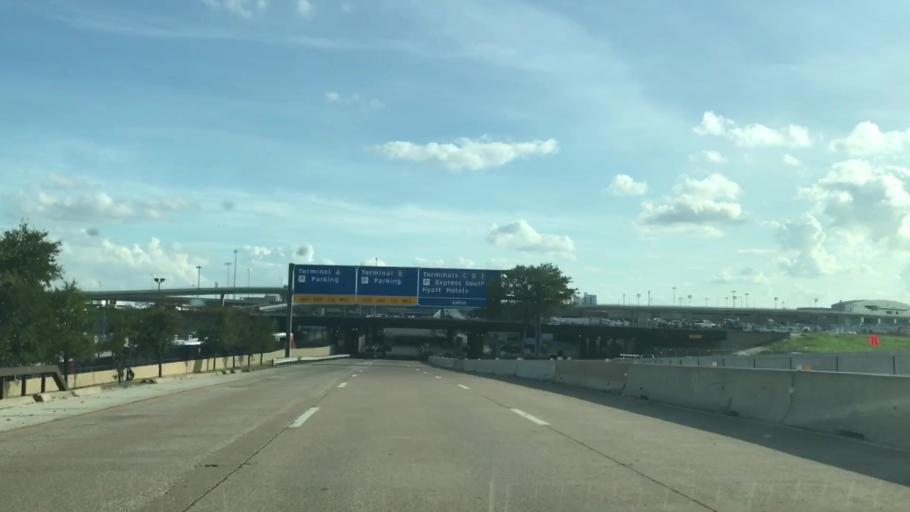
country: US
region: Texas
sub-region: Tarrant County
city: Grapevine
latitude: 32.9117
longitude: -97.0410
